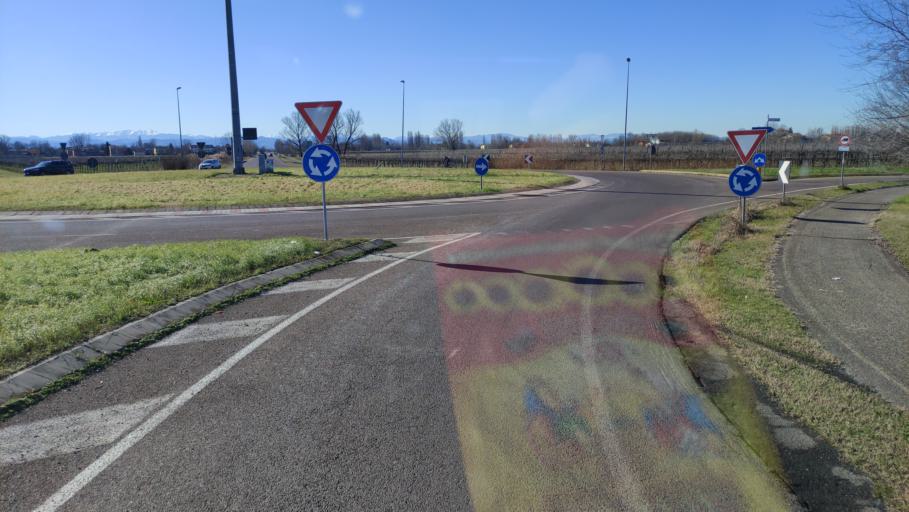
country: IT
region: Emilia-Romagna
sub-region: Provincia di Reggio Emilia
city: San Martino in Rio
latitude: 44.7426
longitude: 10.7754
